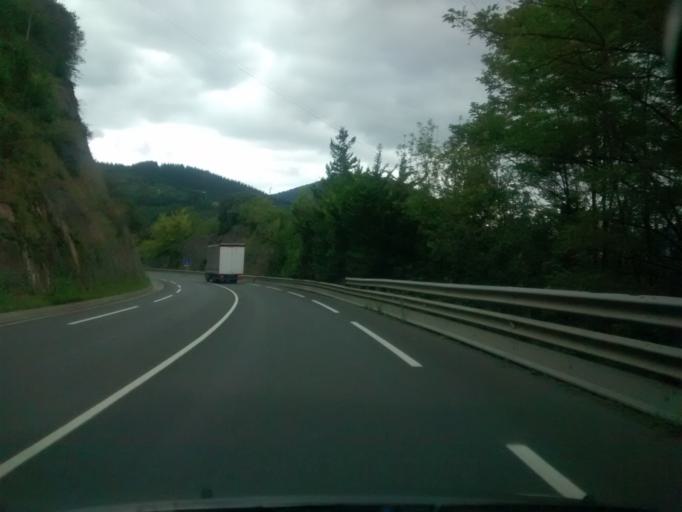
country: ES
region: Basque Country
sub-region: Provincia de Guipuzcoa
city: Arrasate / Mondragon
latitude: 43.0629
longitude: -2.4894
